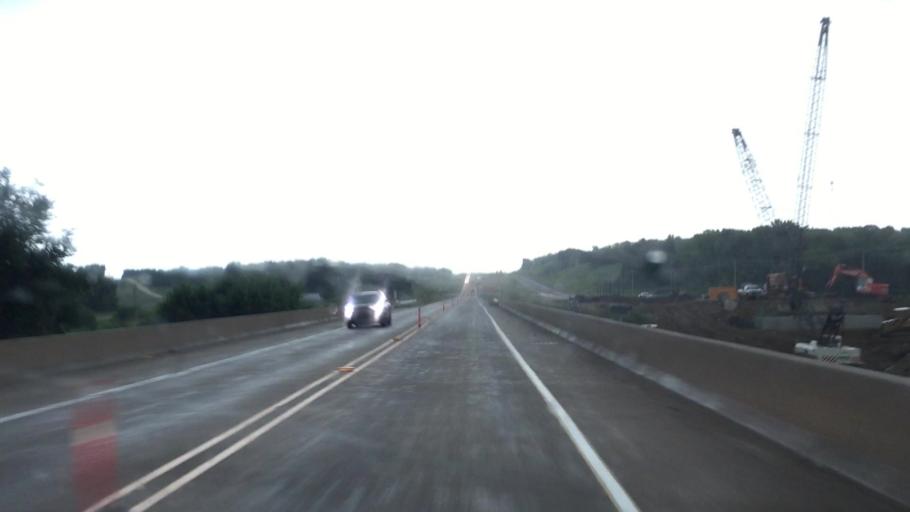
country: US
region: Iowa
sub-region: Henry County
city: Mount Pleasant
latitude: 40.8977
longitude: -91.5550
